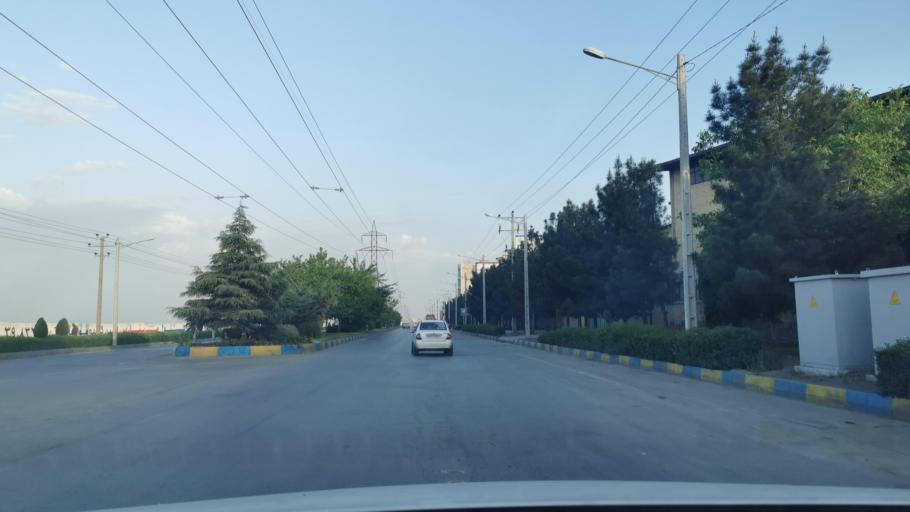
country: IR
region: Razavi Khorasan
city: Torqabeh
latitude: 36.4241
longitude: 59.4248
